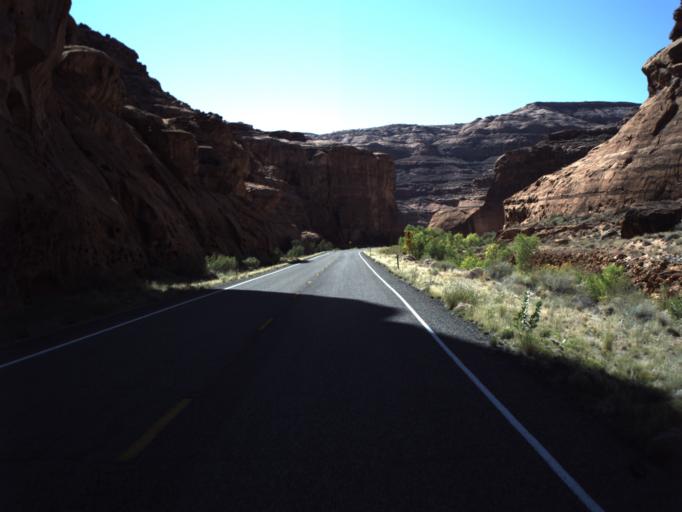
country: US
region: Utah
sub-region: San Juan County
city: Blanding
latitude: 37.9748
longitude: -110.4914
